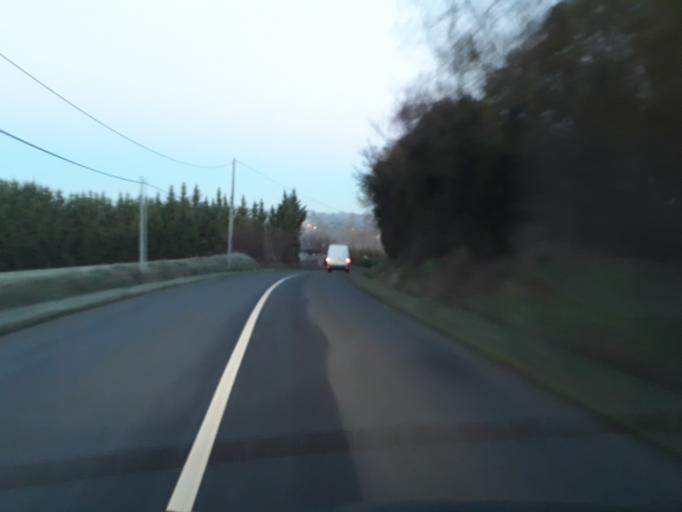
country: FR
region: Midi-Pyrenees
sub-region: Departement du Gers
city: Samatan
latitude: 43.4802
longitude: 0.9385
